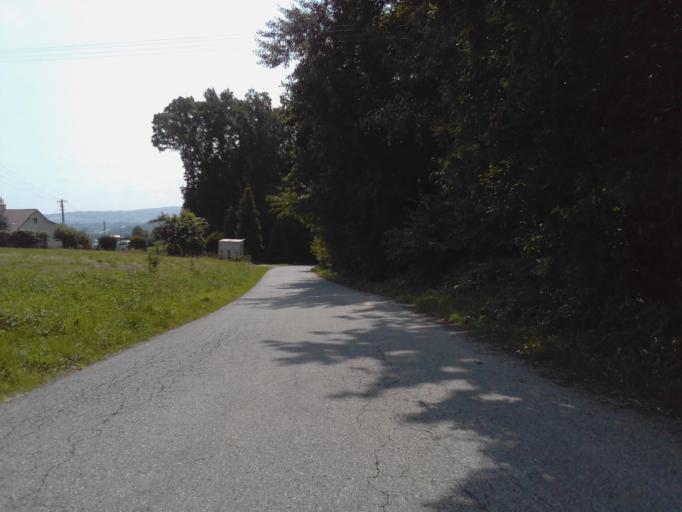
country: PL
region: Subcarpathian Voivodeship
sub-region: Powiat strzyzowski
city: Czudec
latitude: 49.9475
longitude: 21.8100
